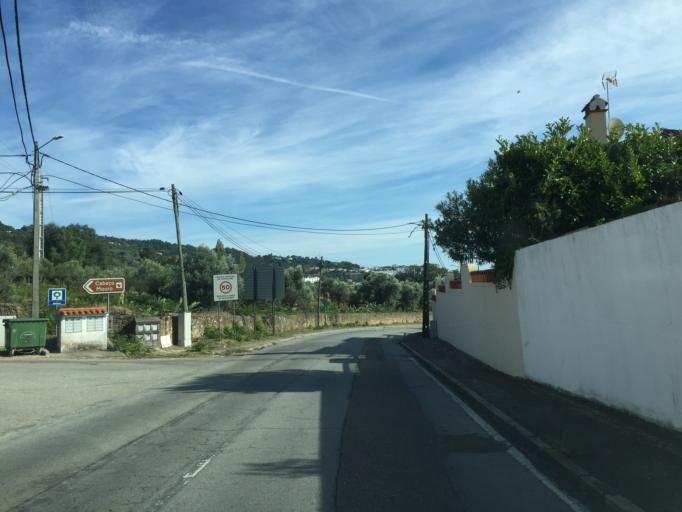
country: PT
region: Portalegre
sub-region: Portalegre
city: Portalegre
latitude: 39.3099
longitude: -7.4397
